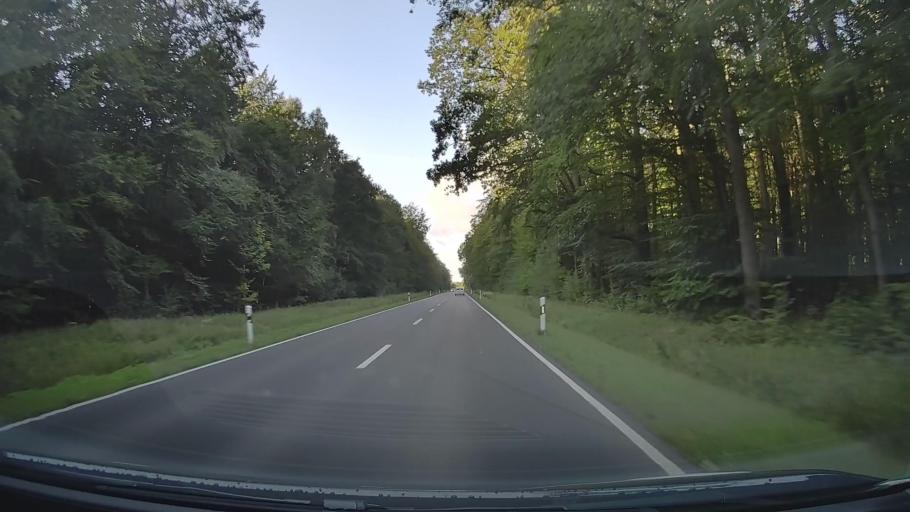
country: DE
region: Mecklenburg-Vorpommern
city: Steinhagen
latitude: 54.2041
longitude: 13.0098
